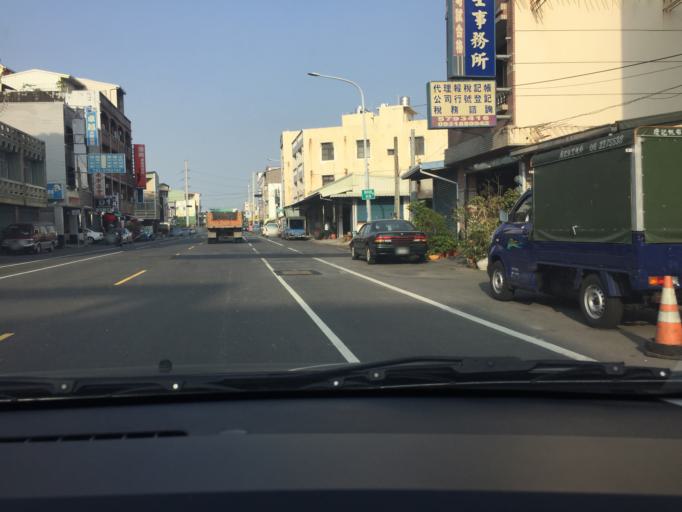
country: TW
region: Taiwan
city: Xinying
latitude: 23.1945
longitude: 120.3164
